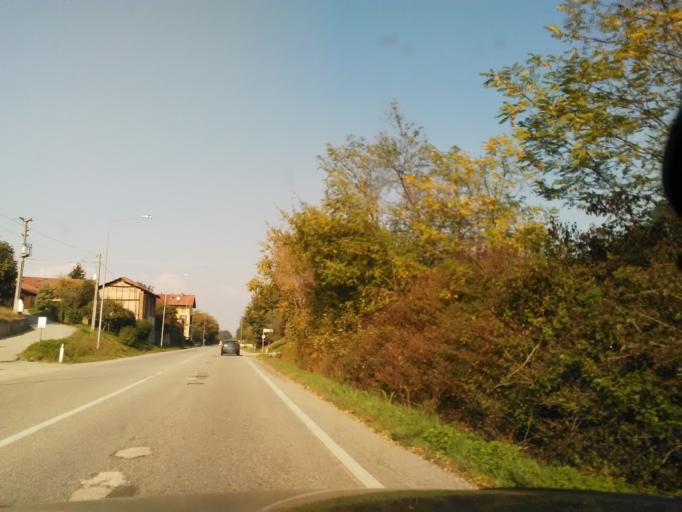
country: IT
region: Piedmont
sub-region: Provincia di Biella
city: Salussola
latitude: 45.4375
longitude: 8.1122
